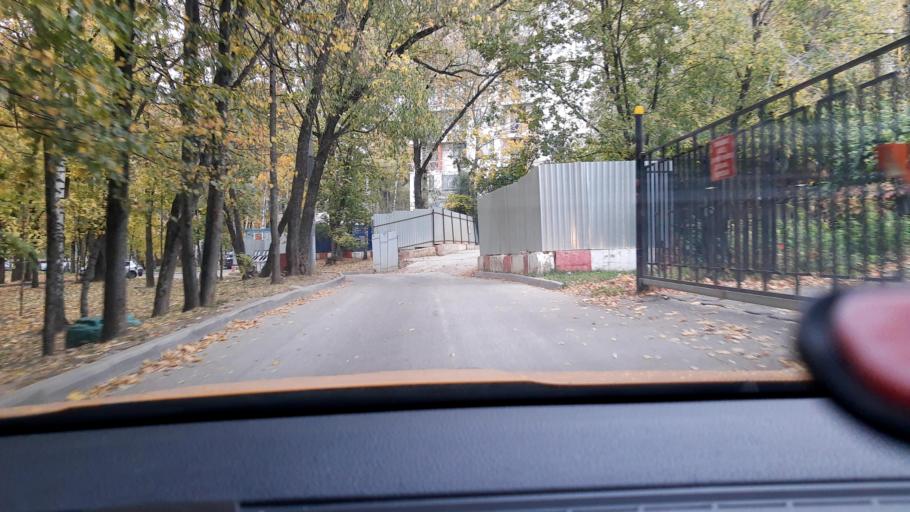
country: RU
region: Moskovskaya
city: Bol'shaya Setun'
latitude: 55.7232
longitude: 37.4311
